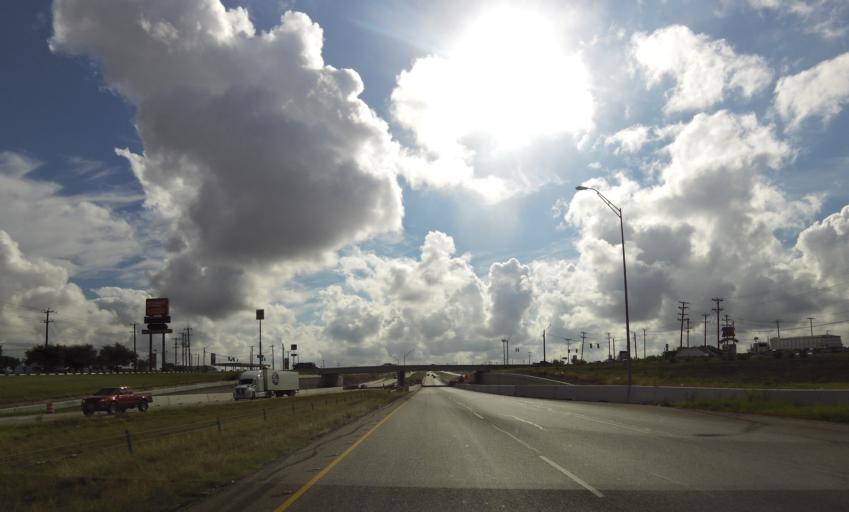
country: US
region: Texas
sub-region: Bexar County
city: Kirby
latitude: 29.4445
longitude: -98.3625
